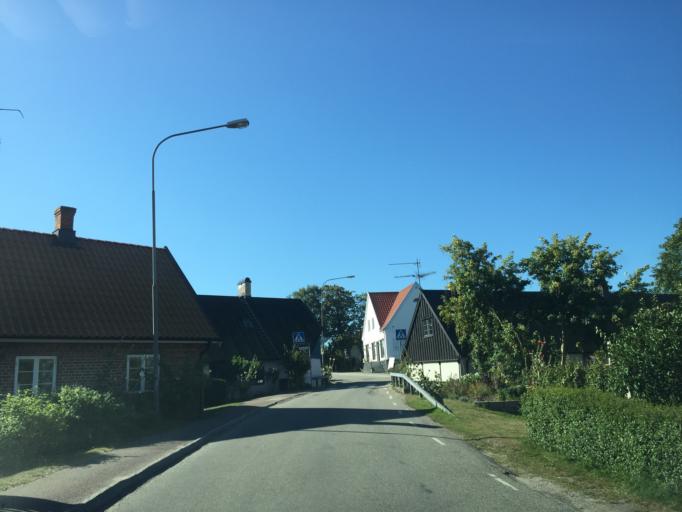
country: SE
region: Skane
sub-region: Ystads Kommun
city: Kopingebro
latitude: 55.3861
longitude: 14.0653
